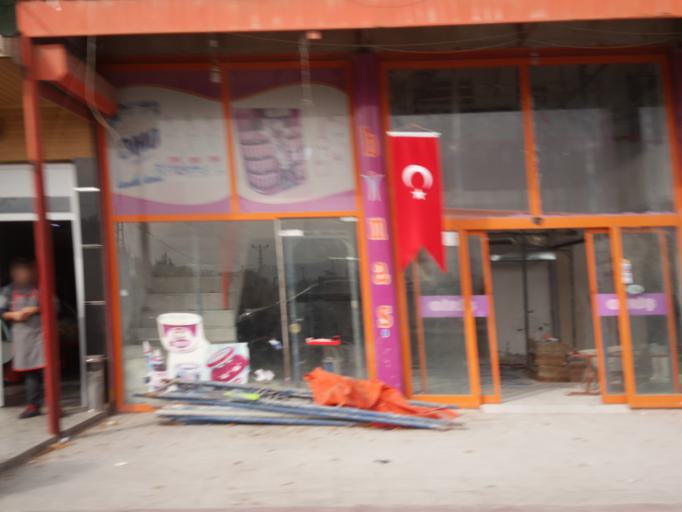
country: TR
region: Kirikkale
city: Bahsili
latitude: 39.8147
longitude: 33.4721
